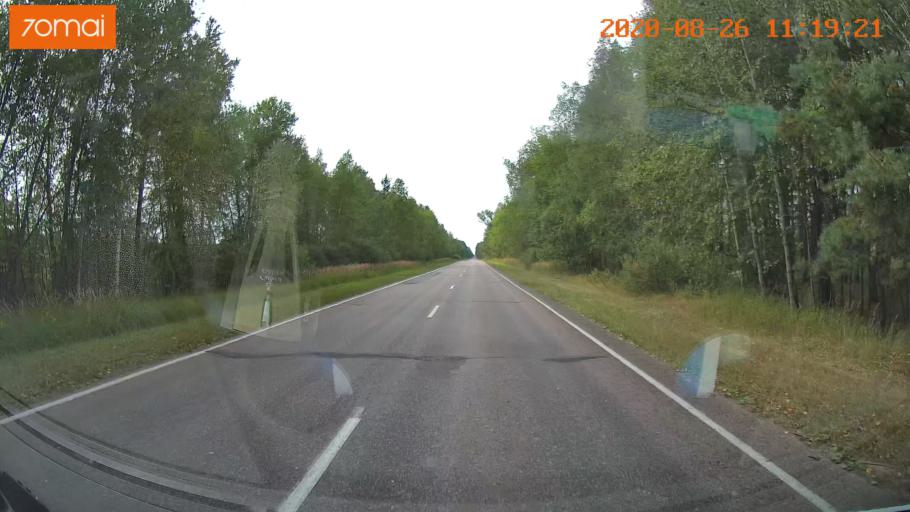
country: RU
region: Rjazan
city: Shilovo
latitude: 54.4001
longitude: 41.0812
